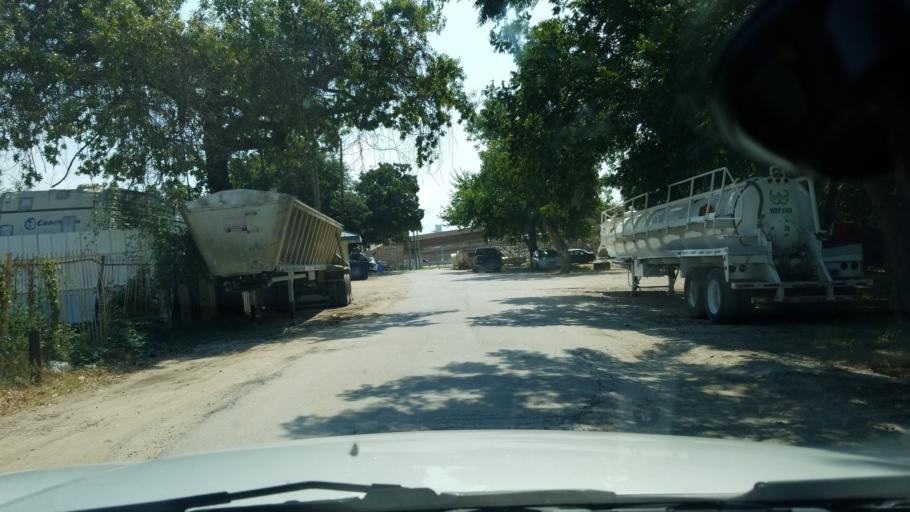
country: US
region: Texas
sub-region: Dallas County
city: Irving
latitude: 32.8604
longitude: -96.9042
